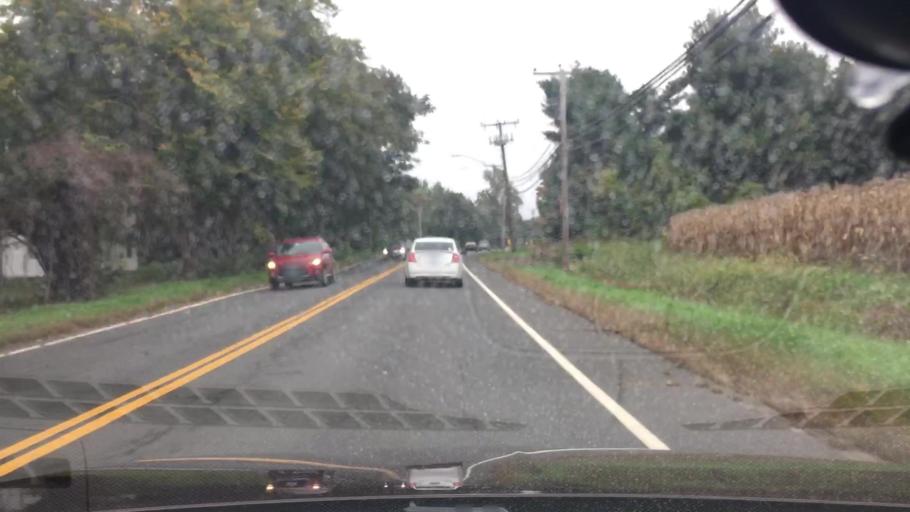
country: US
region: Connecticut
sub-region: Hartford County
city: South Windsor
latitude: 41.8329
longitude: -72.5559
